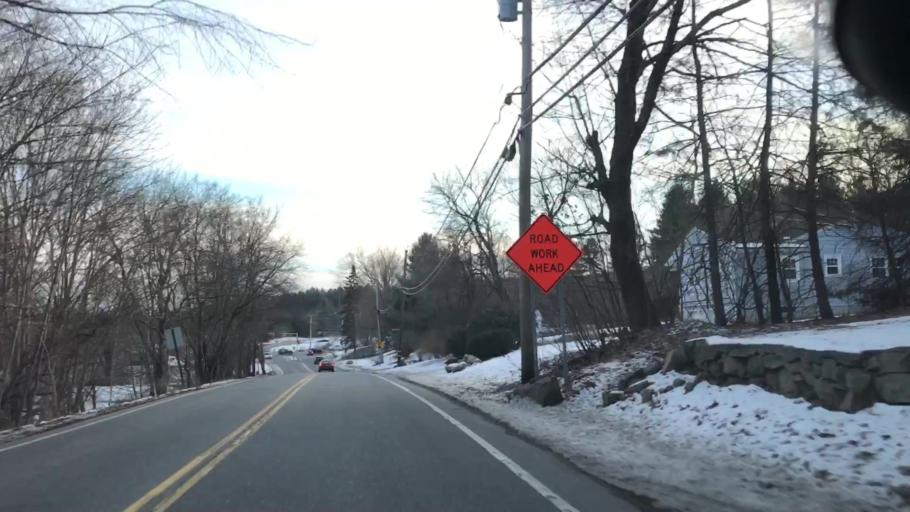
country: US
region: New Hampshire
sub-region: Hillsborough County
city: Bedford
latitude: 42.9400
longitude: -71.5270
